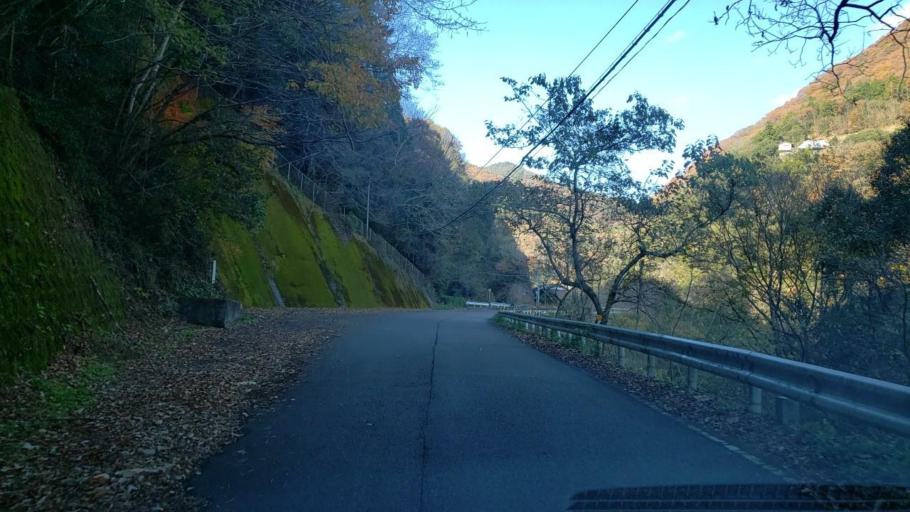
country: JP
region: Tokushima
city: Wakimachi
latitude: 34.0911
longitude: 134.0680
